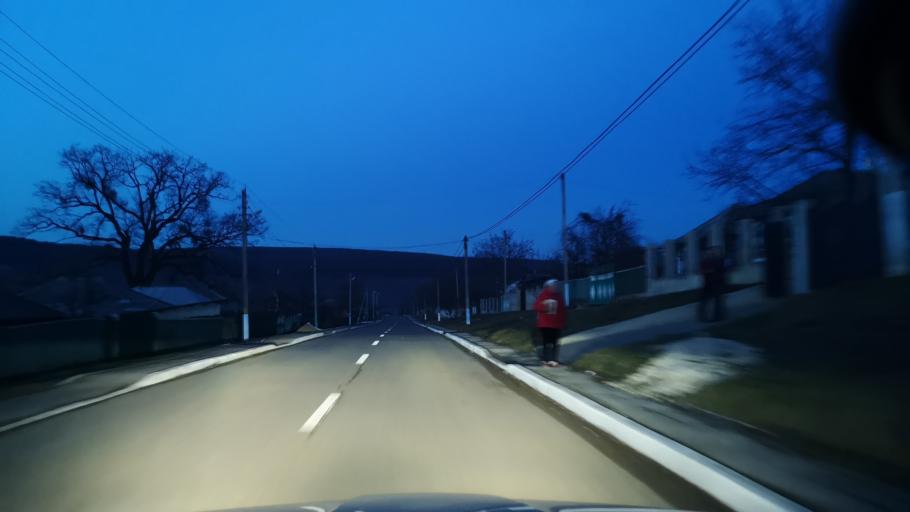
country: MD
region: Orhei
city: Orhei
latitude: 47.3364
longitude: 28.6569
